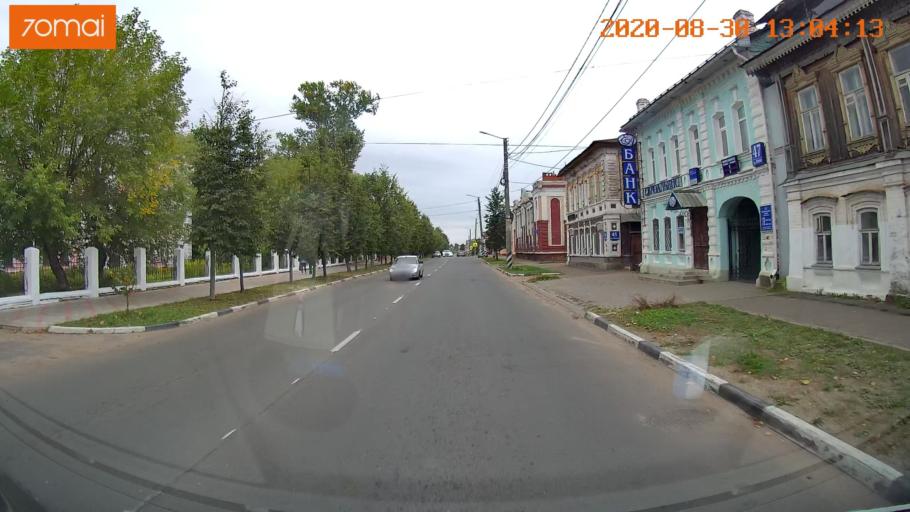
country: RU
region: Ivanovo
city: Kineshma
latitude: 57.4445
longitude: 42.1590
